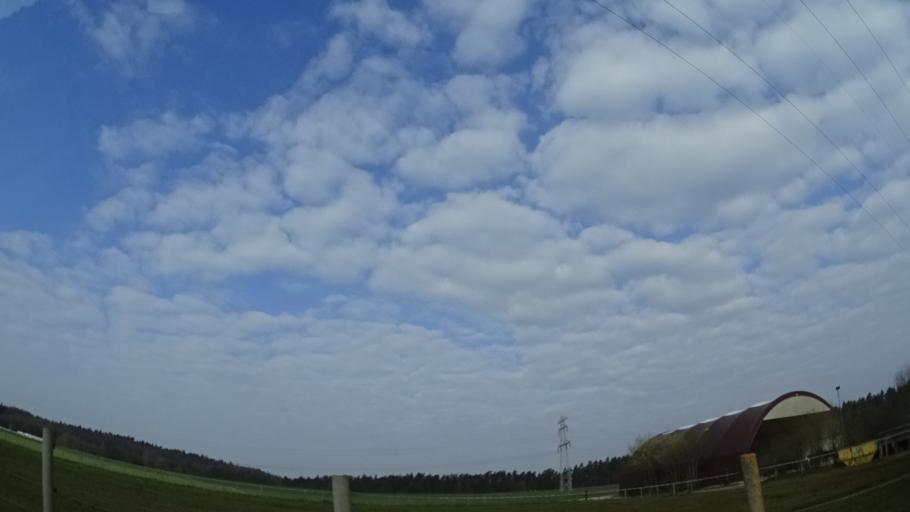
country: DE
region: Bavaria
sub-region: Regierungsbezirk Mittelfranken
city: Altdorf
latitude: 49.3991
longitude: 11.3336
